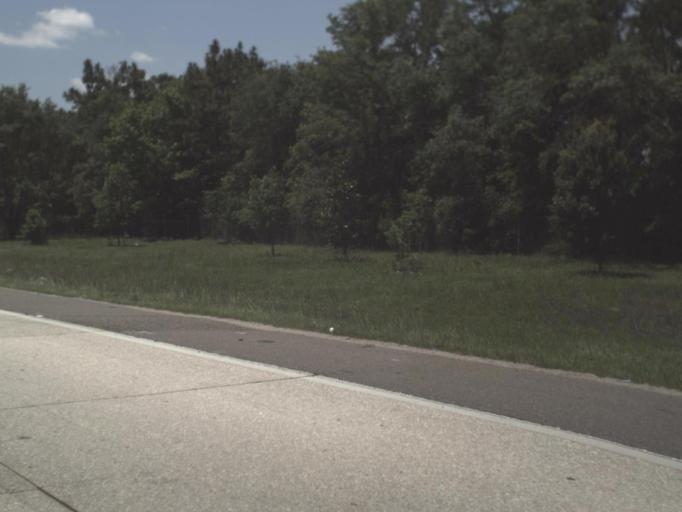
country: US
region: Florida
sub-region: Duval County
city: Jacksonville
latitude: 30.4263
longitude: -81.6566
